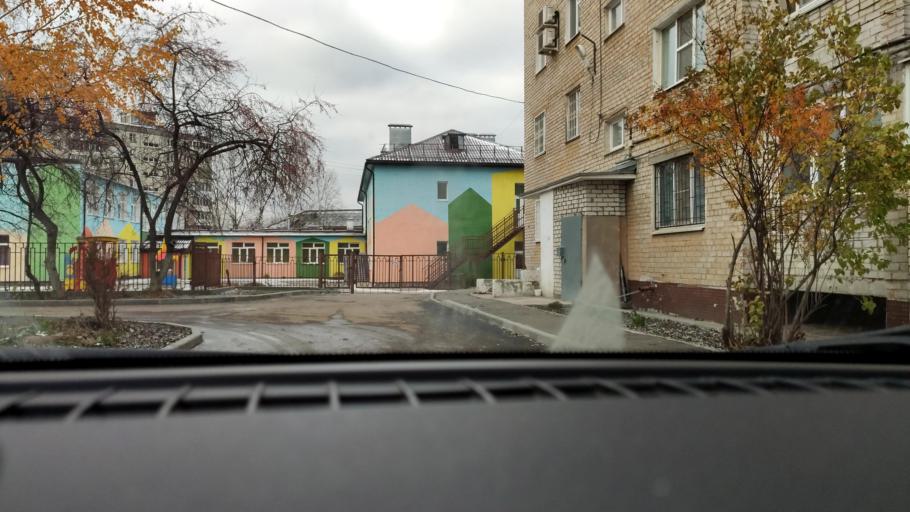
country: RU
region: Perm
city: Perm
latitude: 57.9819
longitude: 56.2155
